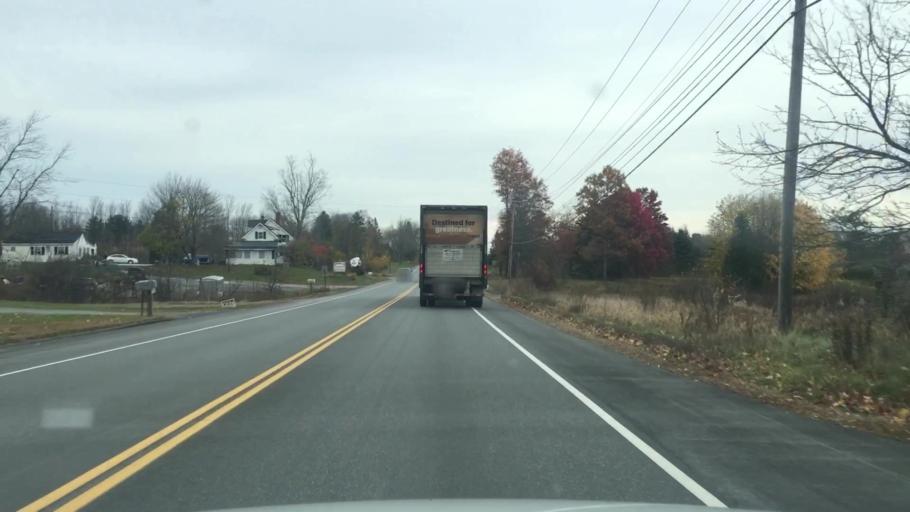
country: US
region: Maine
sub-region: Waldo County
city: Belfast
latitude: 44.4207
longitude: -69.0339
